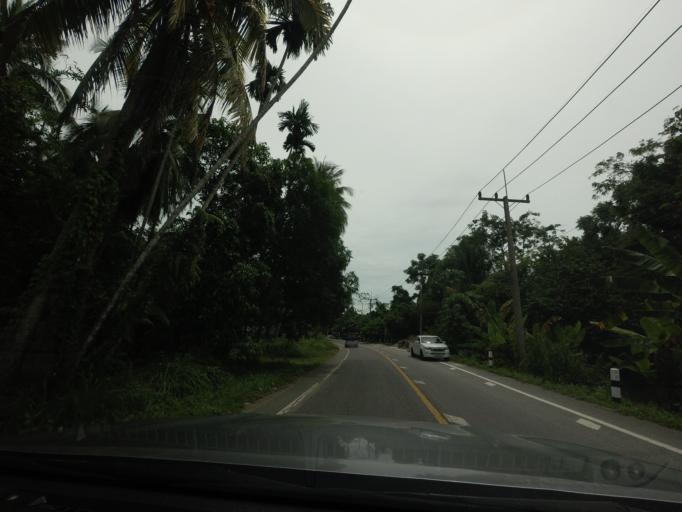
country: TH
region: Pattani
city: Kapho
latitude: 6.6389
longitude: 101.5502
